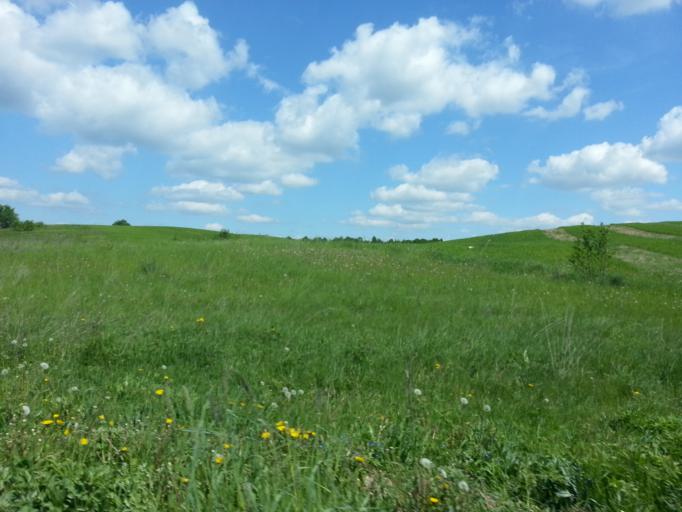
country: LT
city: Trakai
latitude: 54.6807
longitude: 24.9843
